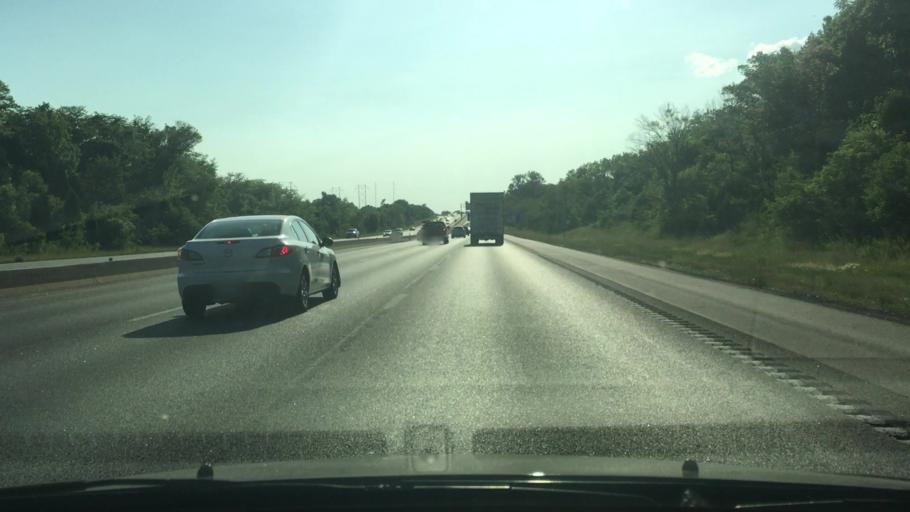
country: US
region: Missouri
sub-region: Jackson County
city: Grandview
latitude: 38.9385
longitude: -94.4976
